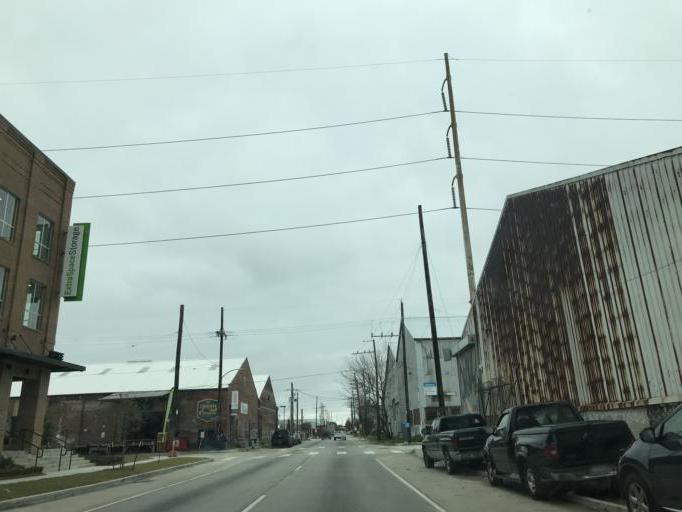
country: US
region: Louisiana
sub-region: Jefferson Parish
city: Gretna
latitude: 29.9306
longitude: -90.0673
